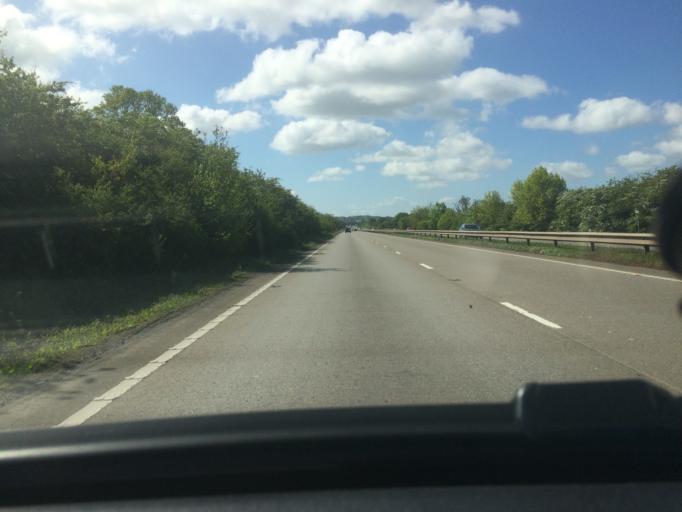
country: GB
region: Wales
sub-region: Wrexham
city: Rossett
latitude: 53.1309
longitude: -2.9474
